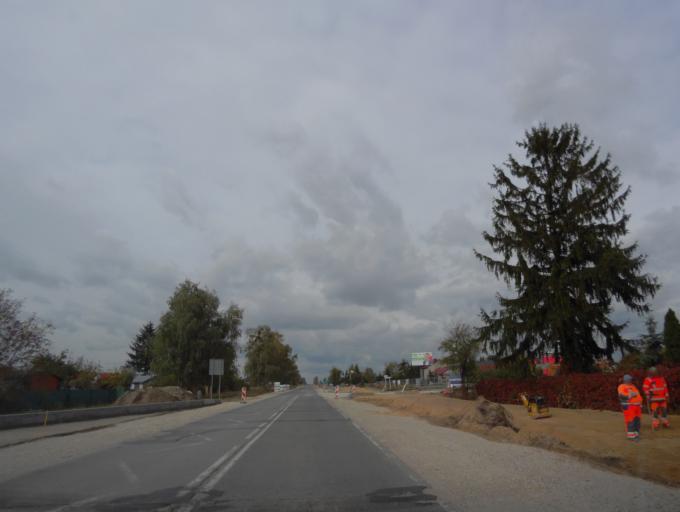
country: PL
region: Lublin Voivodeship
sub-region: Powiat wlodawski
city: Wlodawa
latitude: 51.5513
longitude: 23.5360
